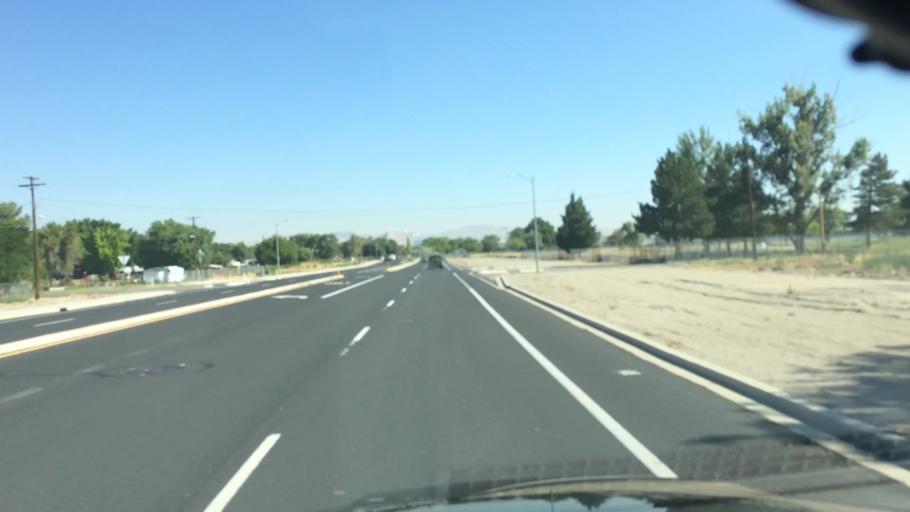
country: US
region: Nevada
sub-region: Washoe County
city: Sparks
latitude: 39.4865
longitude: -119.7759
